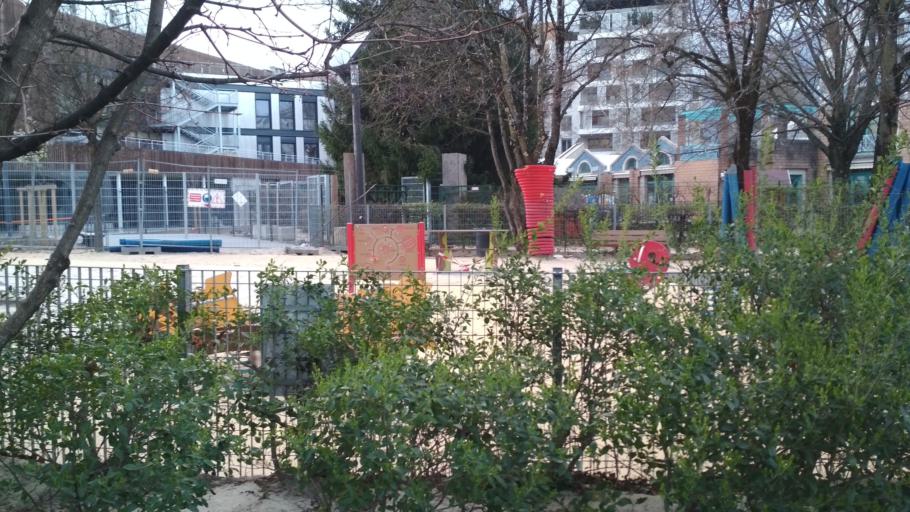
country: FR
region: Rhone-Alpes
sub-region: Departement de l'Isere
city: Grenoble
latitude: 45.1846
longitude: 5.7275
